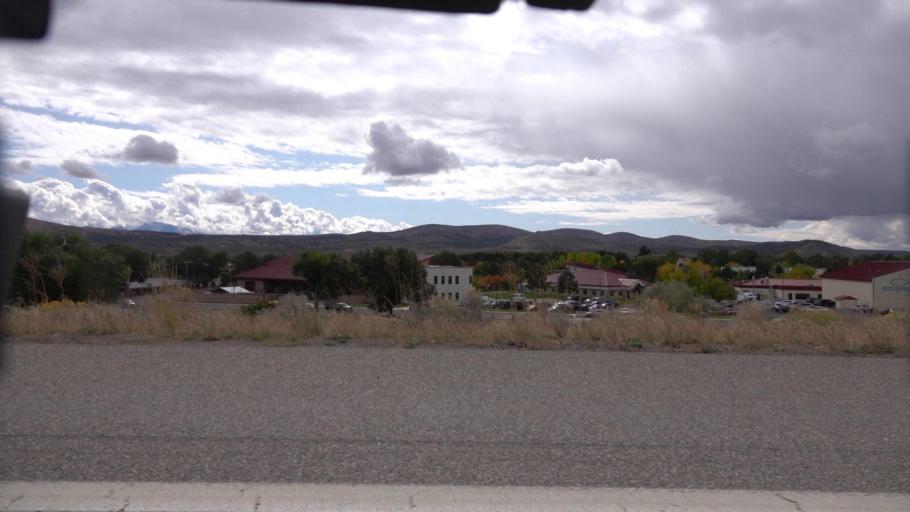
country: US
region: Nevada
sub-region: Elko County
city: Elko
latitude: 40.8454
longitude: -115.7669
